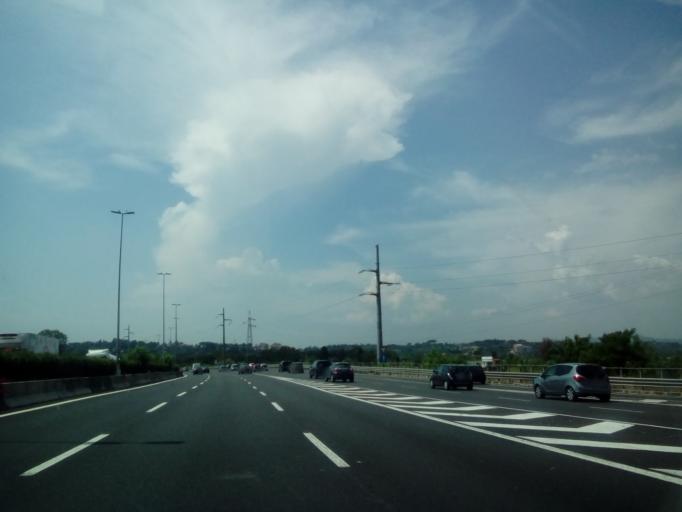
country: IT
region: Latium
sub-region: Citta metropolitana di Roma Capitale
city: Monte Caminetto
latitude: 41.9897
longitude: 12.5114
